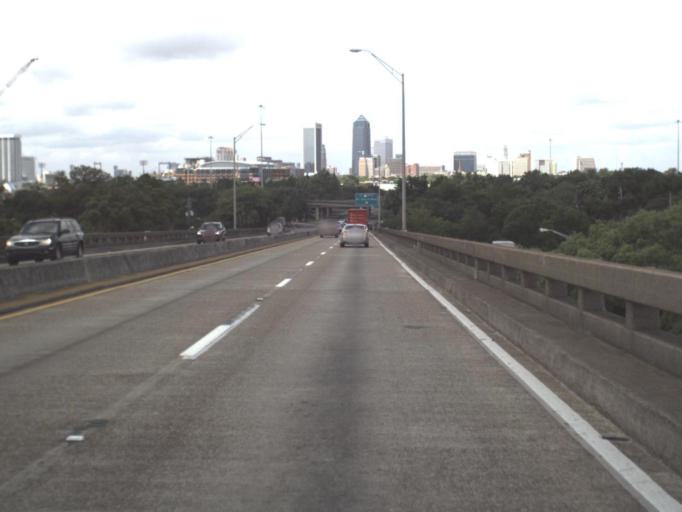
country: US
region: Florida
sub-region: Duval County
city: Jacksonville
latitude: 30.3272
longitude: -81.6322
